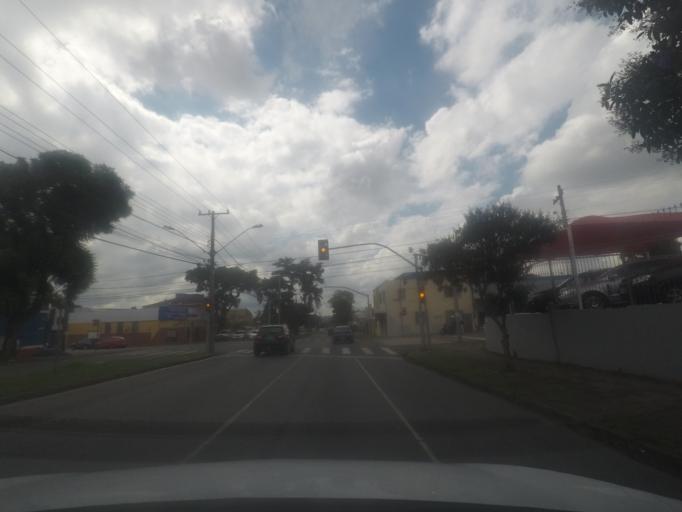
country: BR
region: Parana
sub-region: Curitiba
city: Curitiba
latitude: -25.4538
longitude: -49.2656
